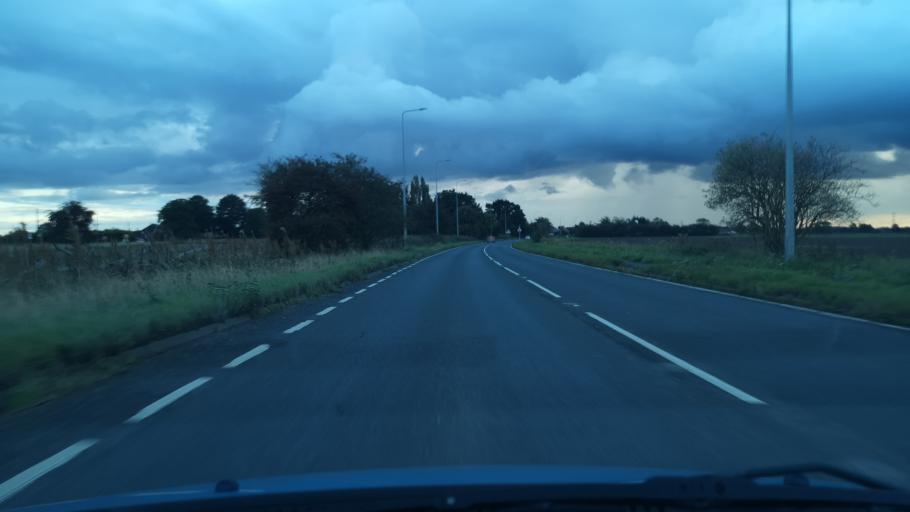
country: GB
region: England
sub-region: North Lincolnshire
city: Gunness
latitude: 53.5822
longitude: -0.7381
